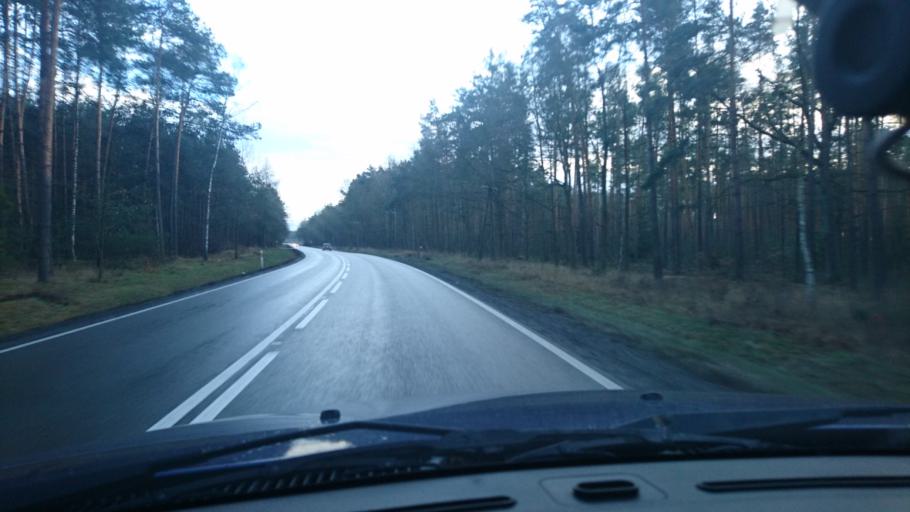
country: PL
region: Greater Poland Voivodeship
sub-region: Powiat kepinski
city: Kepno
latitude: 51.3380
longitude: 17.9534
